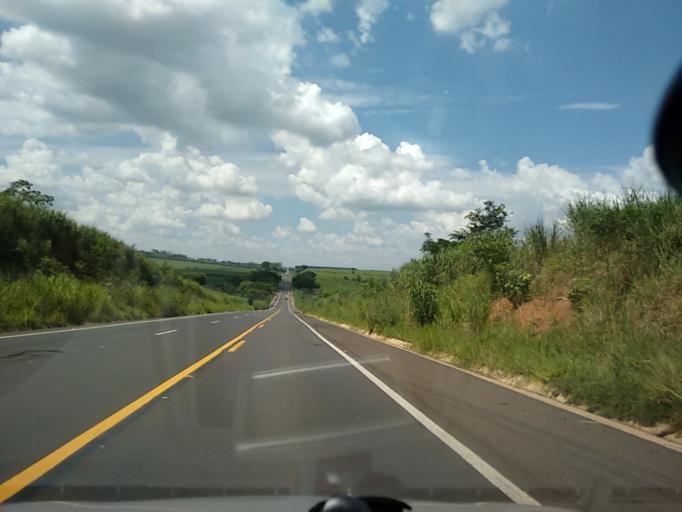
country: BR
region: Sao Paulo
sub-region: Osvaldo Cruz
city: Osvaldo Cruz
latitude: -21.8925
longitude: -50.8748
